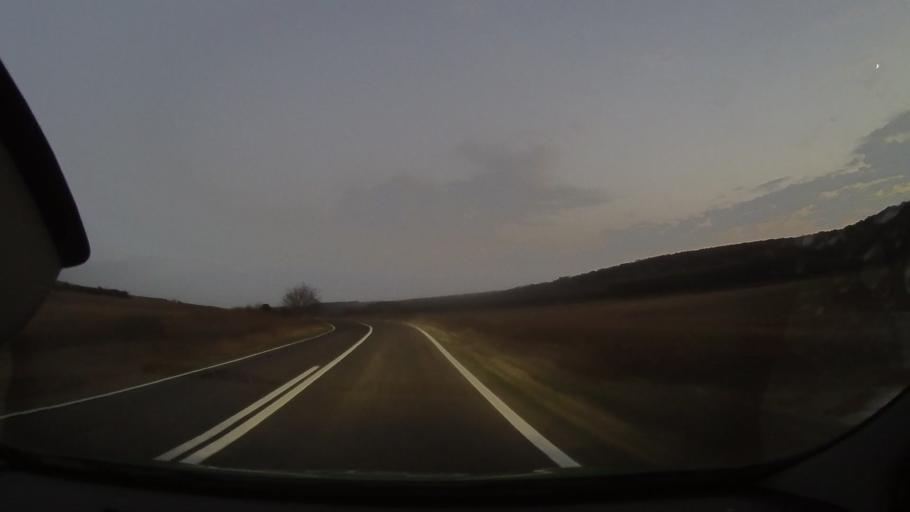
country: RO
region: Constanta
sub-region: Comuna Ion Corvin
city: Ion Corvin
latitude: 44.1061
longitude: 27.7805
